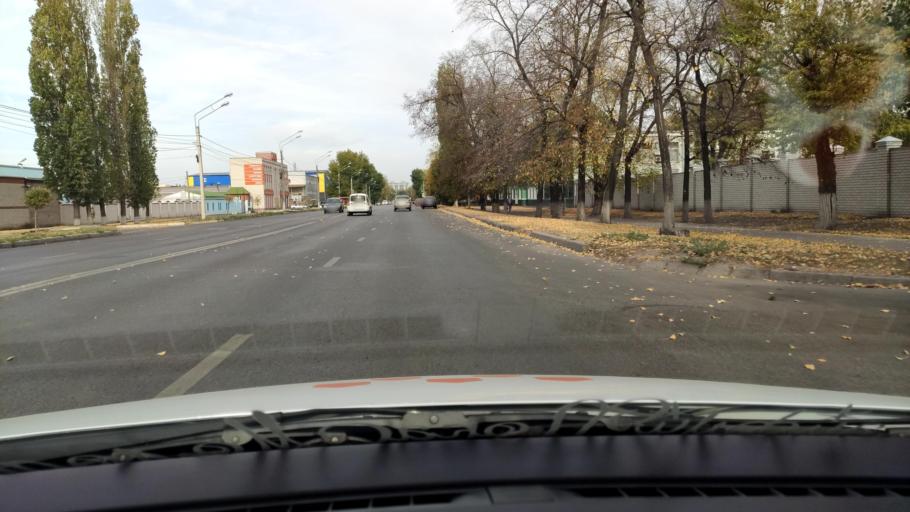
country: RU
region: Voronezj
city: Voronezh
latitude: 51.6503
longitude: 39.2696
